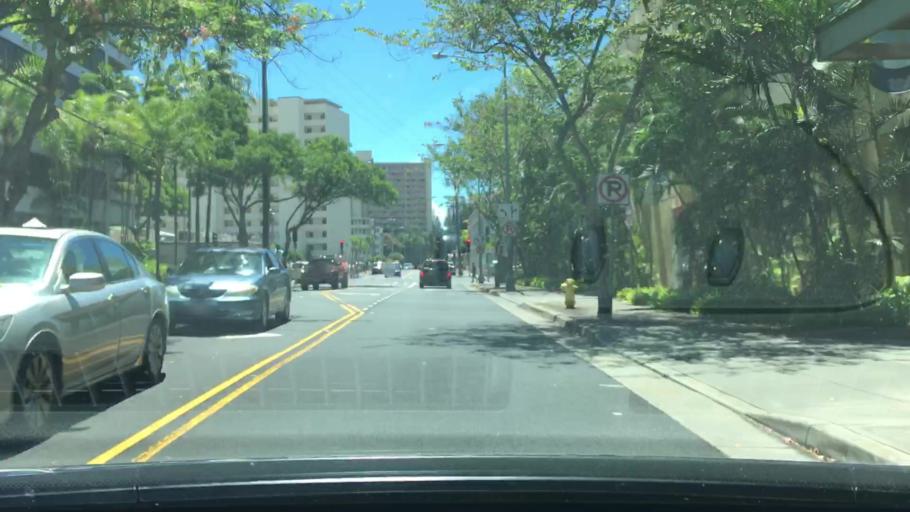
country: US
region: Hawaii
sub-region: Honolulu County
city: Honolulu
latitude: 21.2965
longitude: -157.8420
